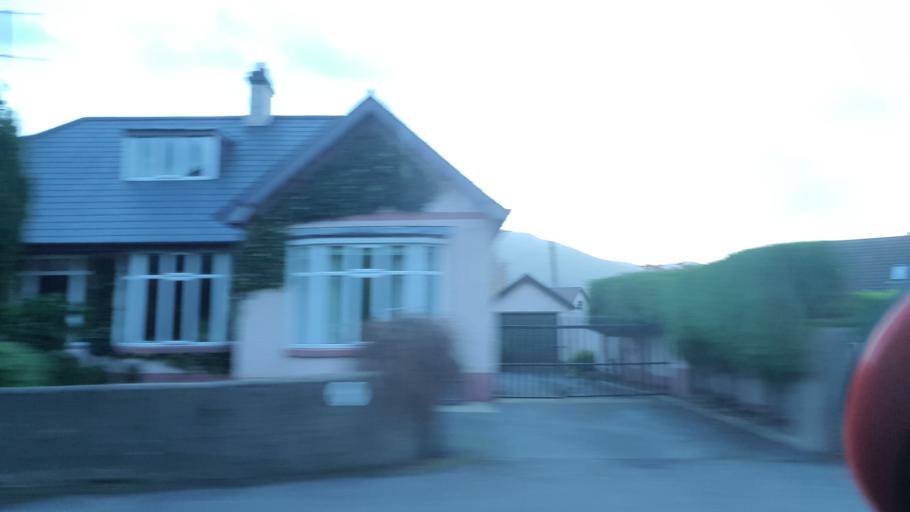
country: GB
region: Northern Ireland
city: Rostrevor
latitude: 54.0764
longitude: -6.1817
